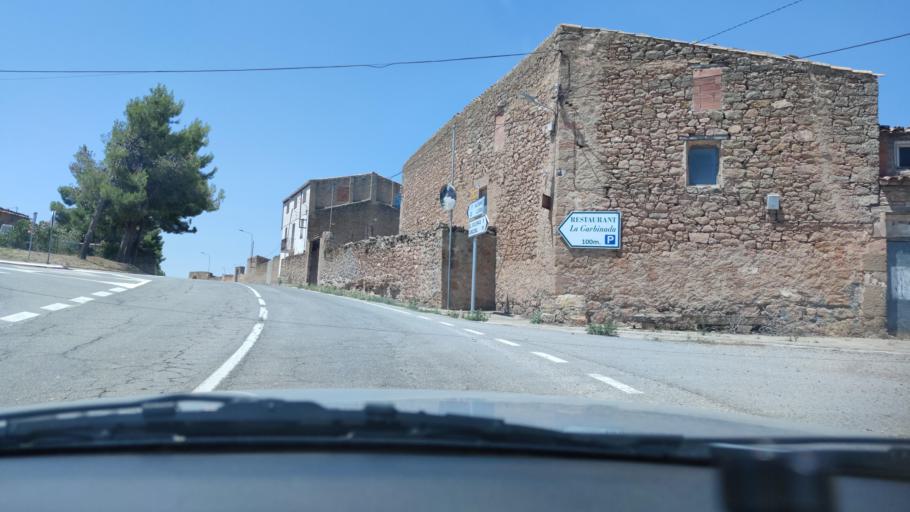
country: ES
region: Catalonia
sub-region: Provincia de Lleida
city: el Cogul
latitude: 41.4338
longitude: 0.6518
